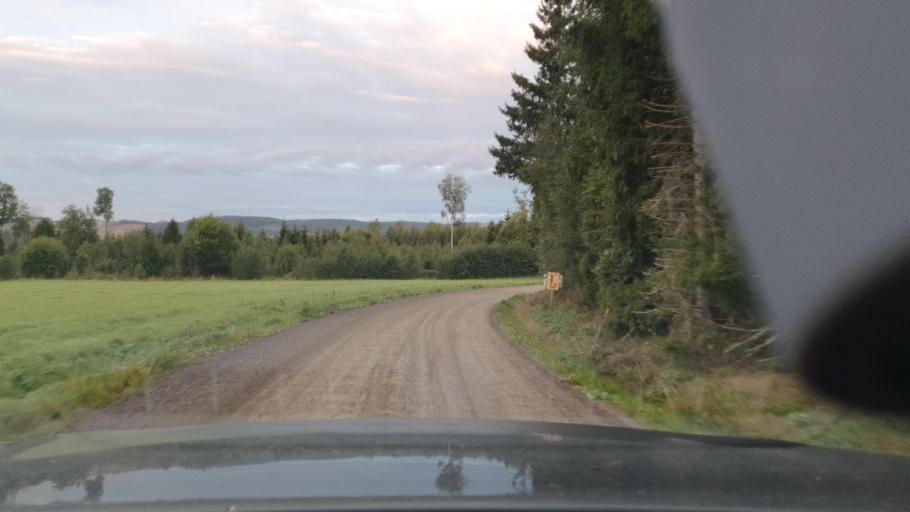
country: SE
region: Vaermland
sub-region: Sunne Kommun
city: Sunne
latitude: 59.8034
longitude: 13.0954
